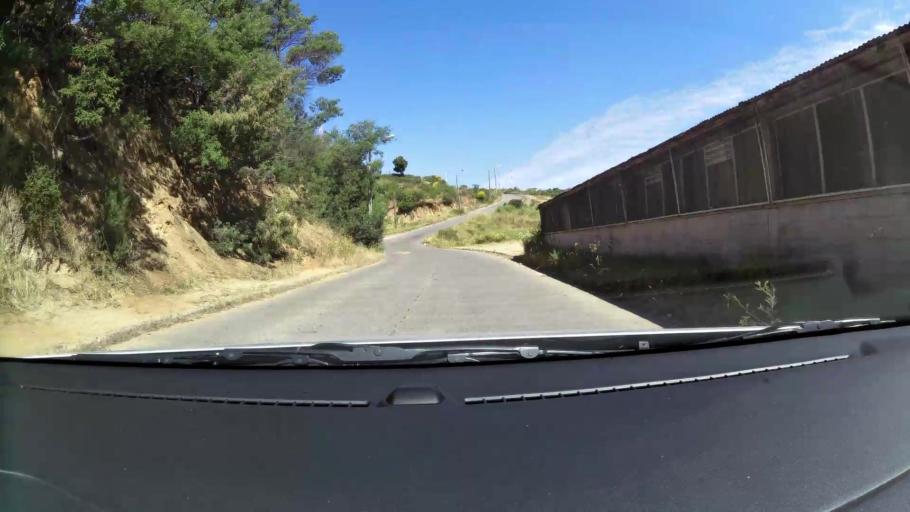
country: CL
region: Valparaiso
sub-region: Provincia de Valparaiso
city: Vina del Mar
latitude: -33.0426
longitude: -71.5698
